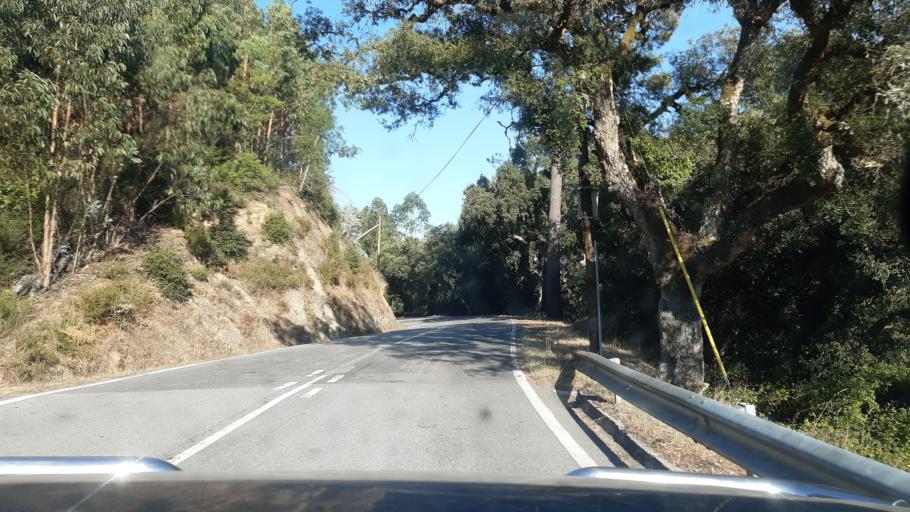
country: PT
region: Aveiro
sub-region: Agueda
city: Agueda
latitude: 40.5621
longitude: -8.4249
